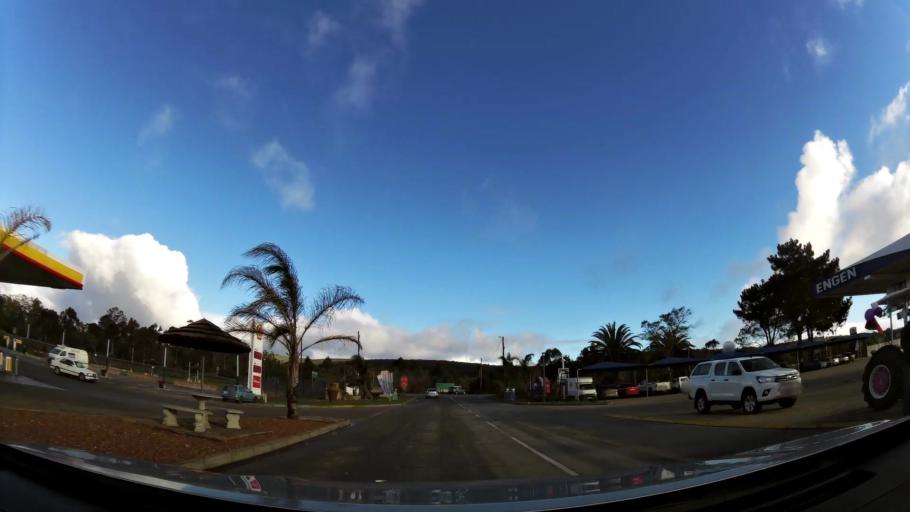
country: ZA
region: Western Cape
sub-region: Eden District Municipality
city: Riversdale
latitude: -34.2117
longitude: 21.5848
